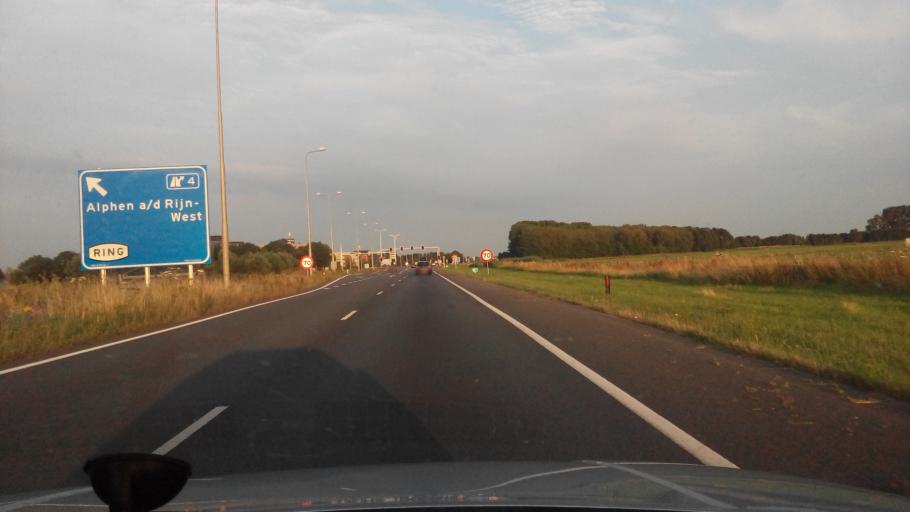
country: NL
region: South Holland
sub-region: Gemeente Alphen aan den Rijn
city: Alphen aan den Rijn
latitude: 52.1247
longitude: 4.6223
